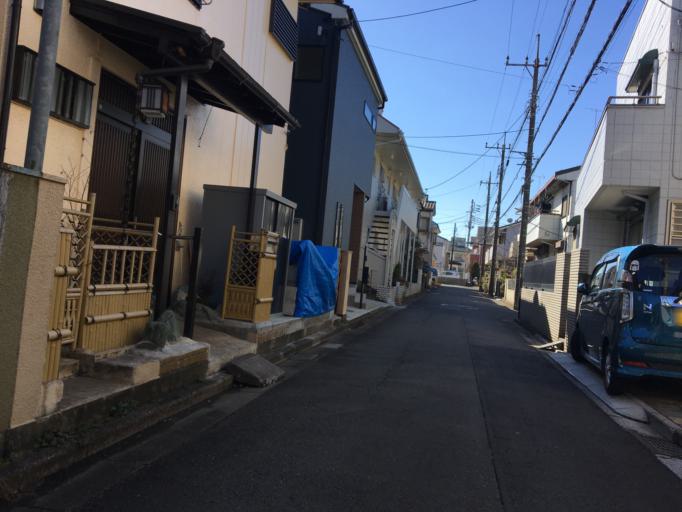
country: JP
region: Saitama
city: Oi
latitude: 35.8359
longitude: 139.5427
